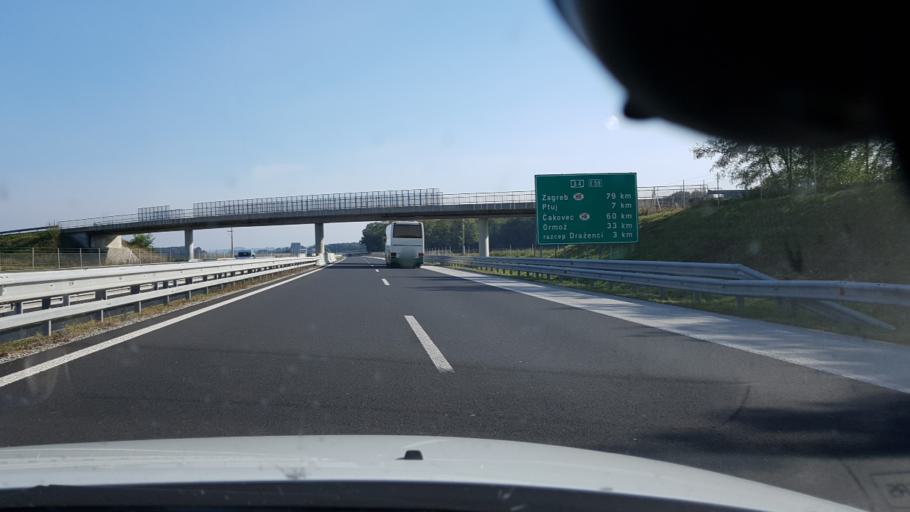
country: SI
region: Kidricevo
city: Kidricevo
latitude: 46.4067
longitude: 15.8189
